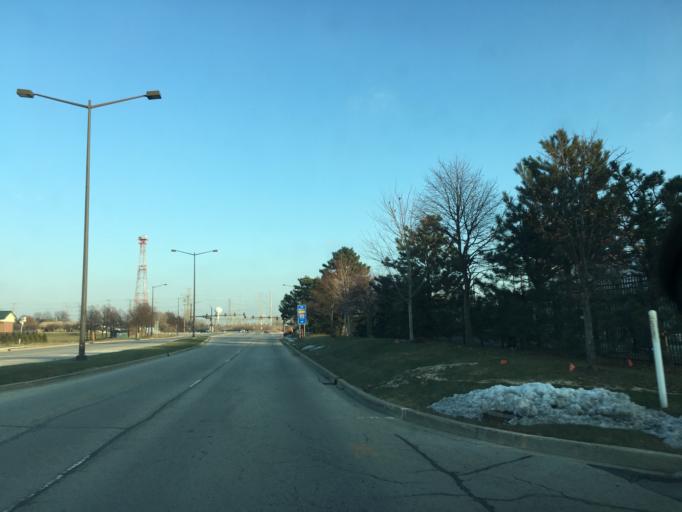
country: US
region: Illinois
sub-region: DuPage County
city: Warrenville
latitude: 41.7981
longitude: -88.2438
